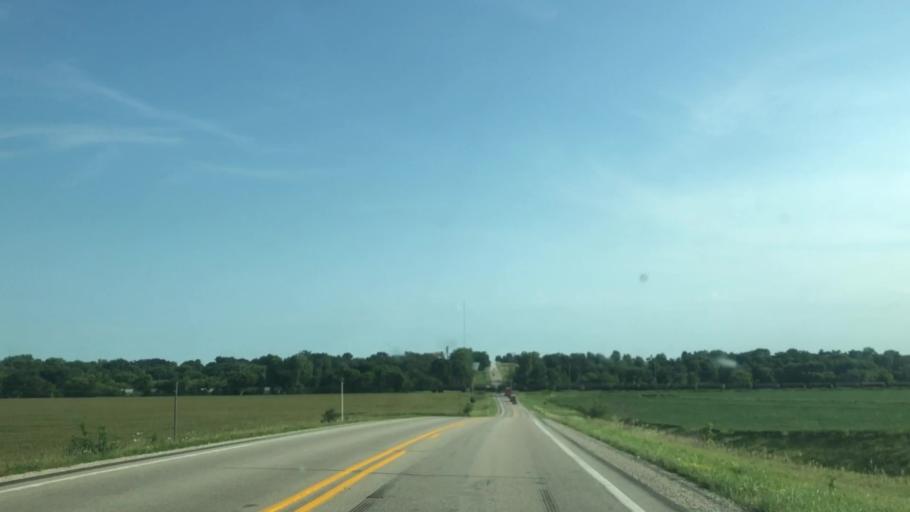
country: US
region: Iowa
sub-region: Marshall County
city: Marshalltown
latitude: 42.0342
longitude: -93.0000
